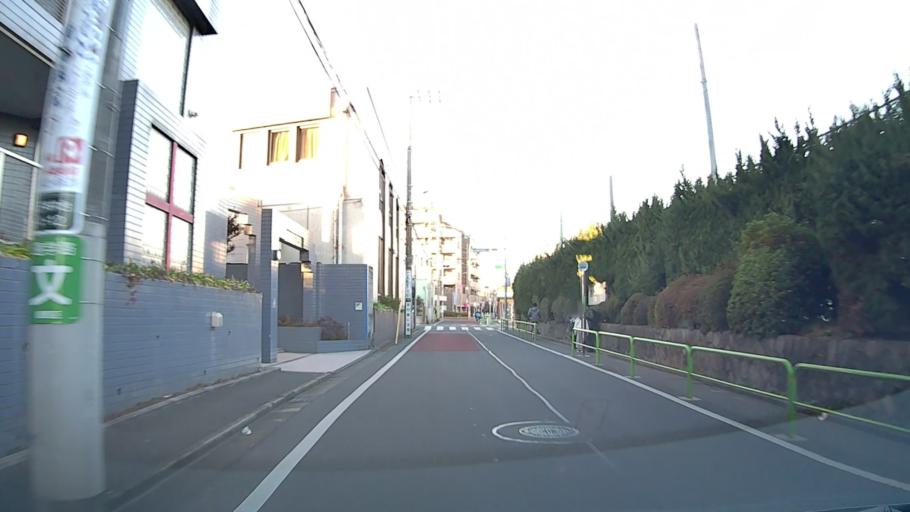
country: JP
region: Tokyo
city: Musashino
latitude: 35.7345
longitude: 139.5897
